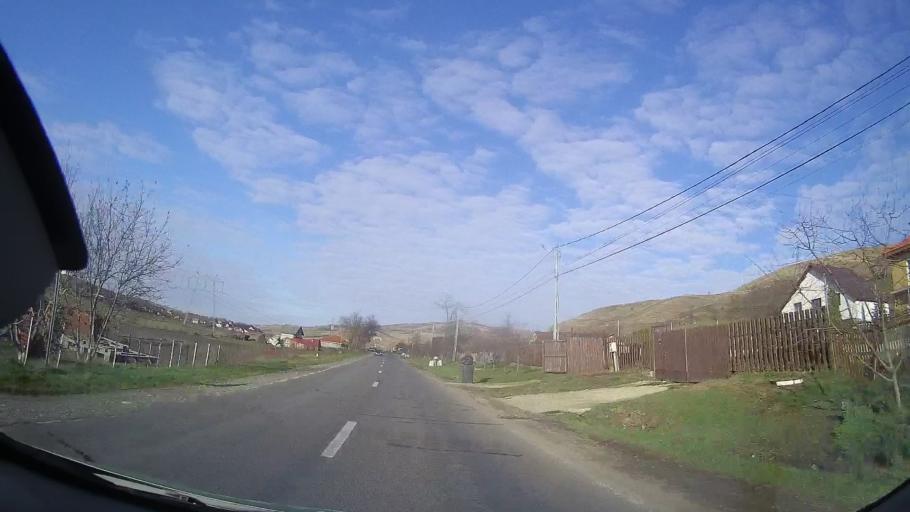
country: RO
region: Cluj
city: Caianu Mic
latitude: 46.8050
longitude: 23.8737
